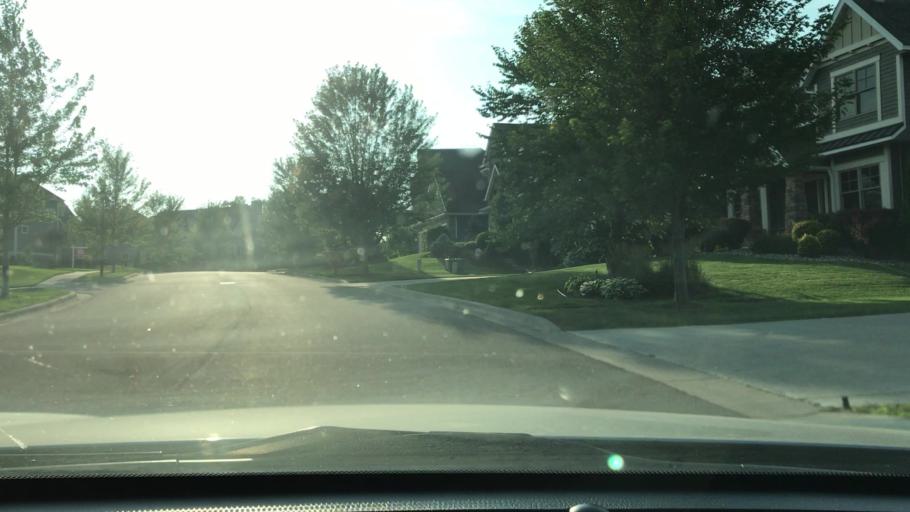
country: US
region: Minnesota
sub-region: Hennepin County
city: Maple Grove
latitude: 45.0538
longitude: -93.4771
